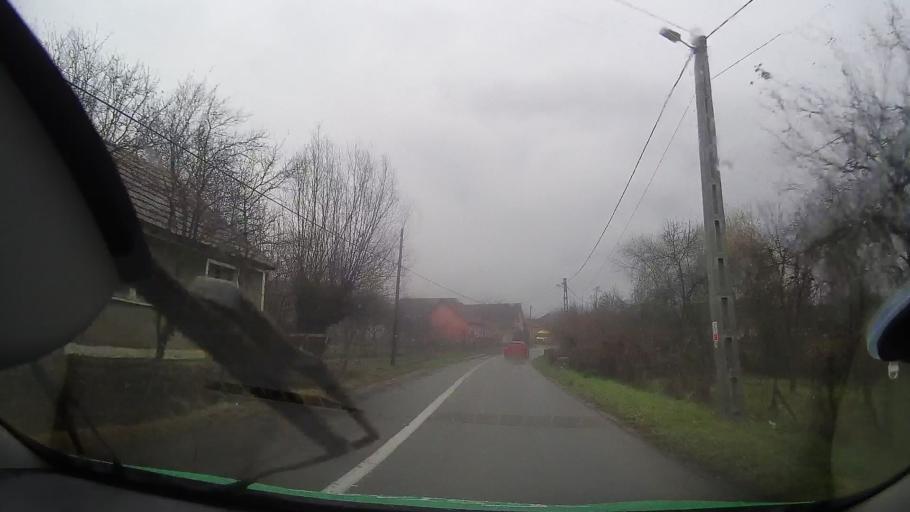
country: RO
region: Bihor
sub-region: Comuna Holod
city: Vintere
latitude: 46.7725
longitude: 22.1370
